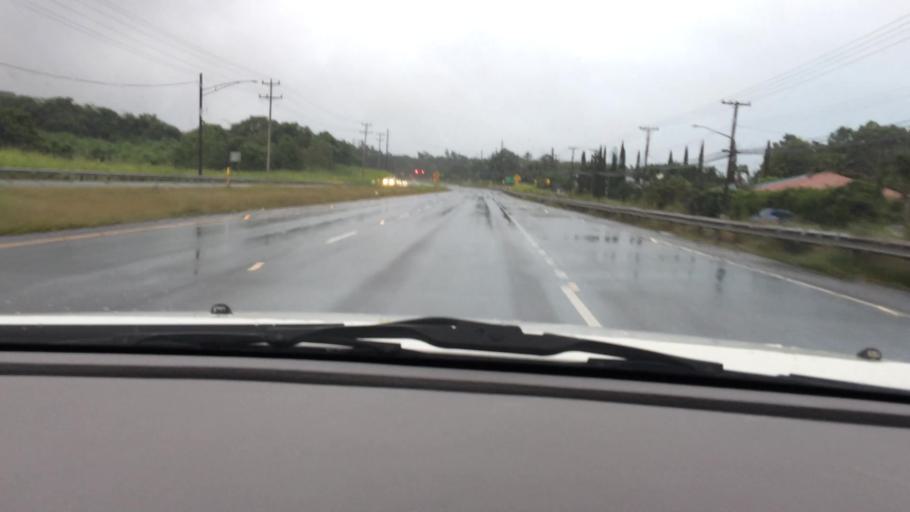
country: US
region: Hawaii
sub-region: Hawaii County
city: Kea'au
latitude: 19.6289
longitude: -155.0393
